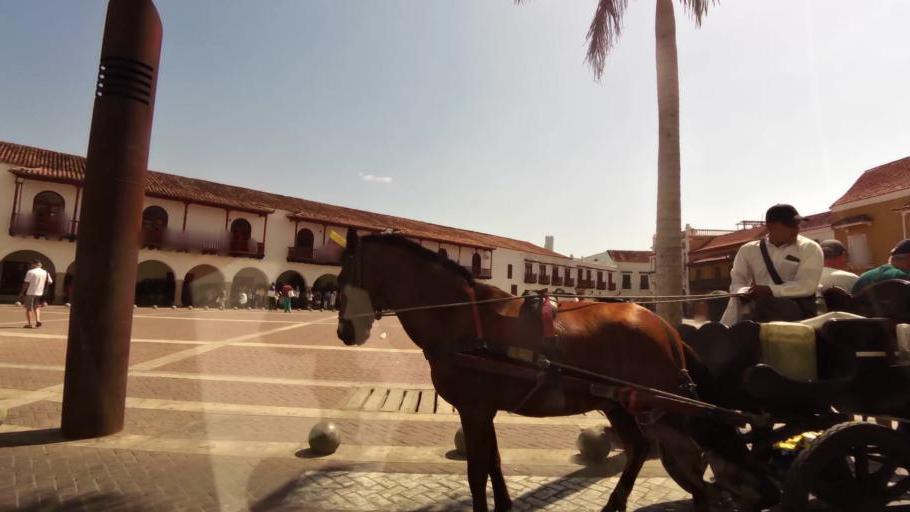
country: CO
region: Bolivar
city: Cartagena
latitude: 10.4224
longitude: -75.5502
